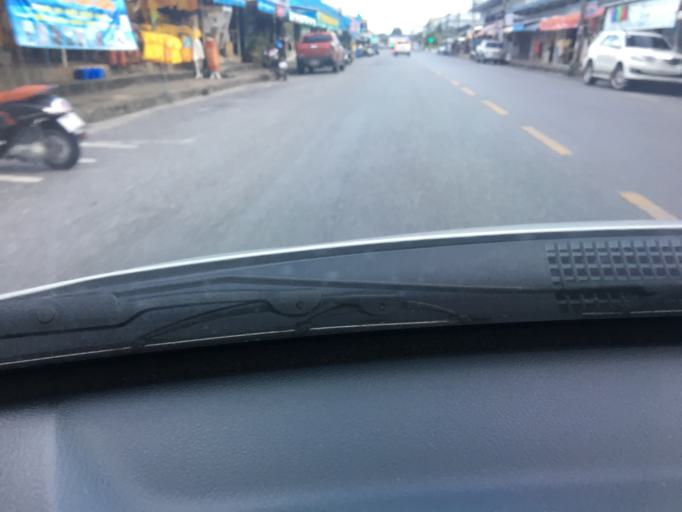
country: TH
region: Phuket
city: Ban Talat Yai
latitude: 7.8813
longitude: 98.3954
